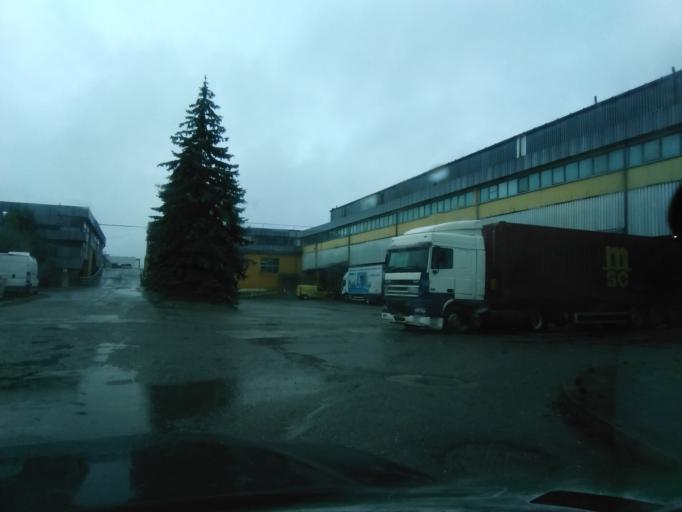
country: PL
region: Subcarpathian Voivodeship
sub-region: Powiat debicki
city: Debica
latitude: 50.0541
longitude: 21.3911
